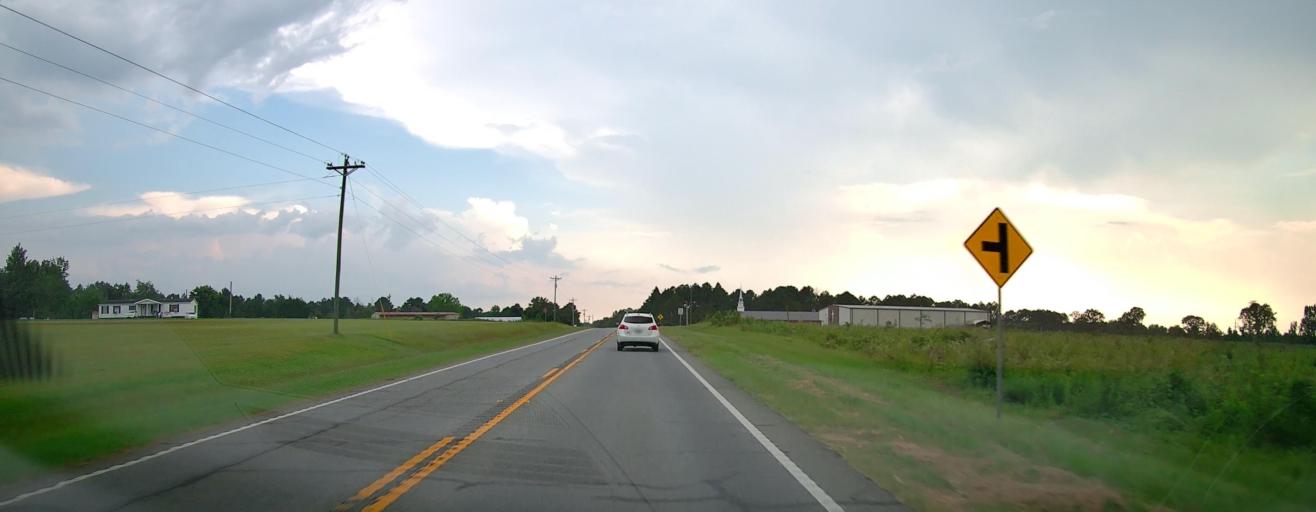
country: US
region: Georgia
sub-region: Laurens County
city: East Dublin
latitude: 32.5667
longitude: -82.8464
